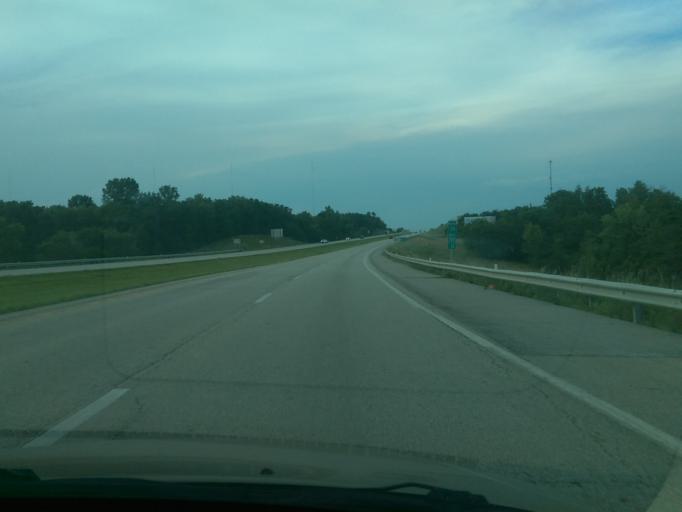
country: US
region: Missouri
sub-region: Andrew County
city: Country Club Village
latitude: 39.8196
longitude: -94.8050
